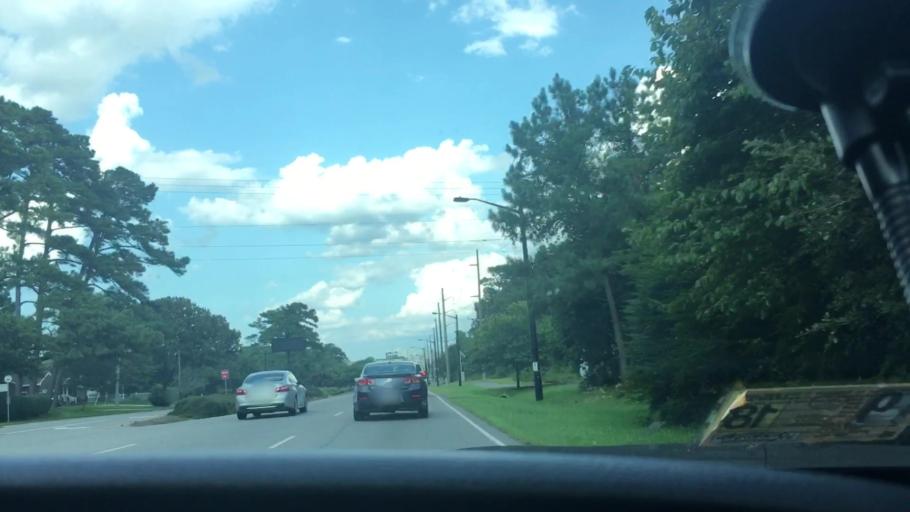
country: US
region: Virginia
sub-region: City of Virginia Beach
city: Virginia Beach
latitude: 36.9069
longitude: -76.1125
